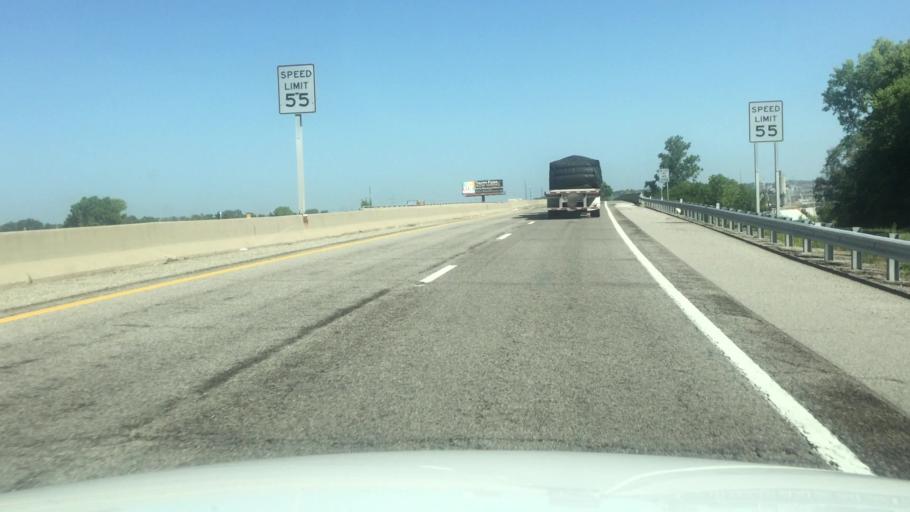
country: US
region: Kansas
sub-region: Doniphan County
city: Elwood
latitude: 39.7368
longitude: -94.8505
